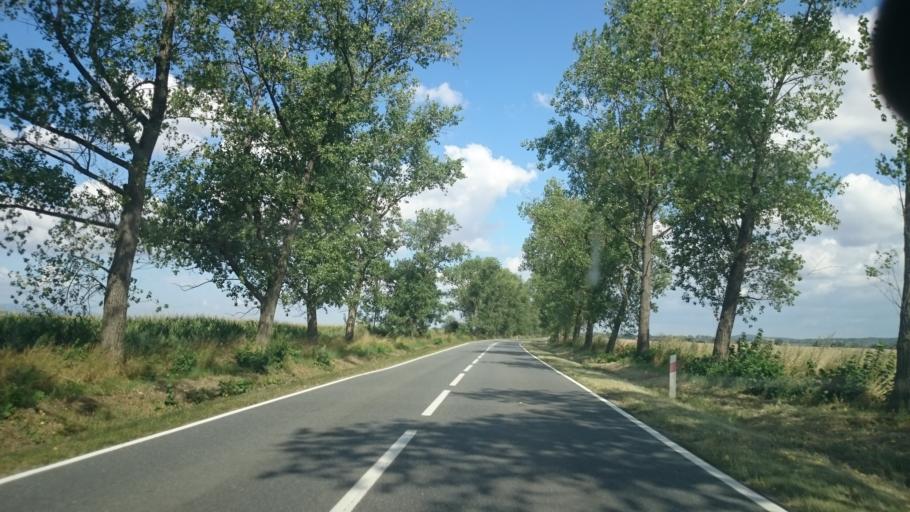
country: PL
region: Lower Silesian Voivodeship
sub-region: Powiat zabkowicki
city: Kamieniec Zabkowicki
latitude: 50.5519
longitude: 16.8573
